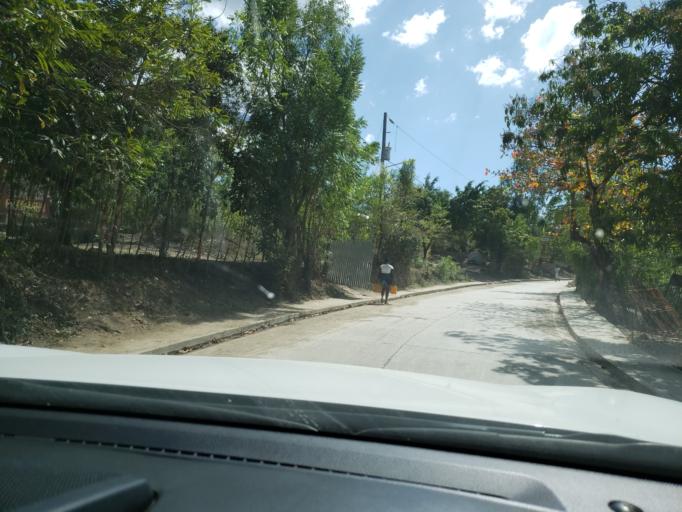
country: HT
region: Grandans
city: Anse-a-Veau
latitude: 18.4528
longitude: -73.3796
